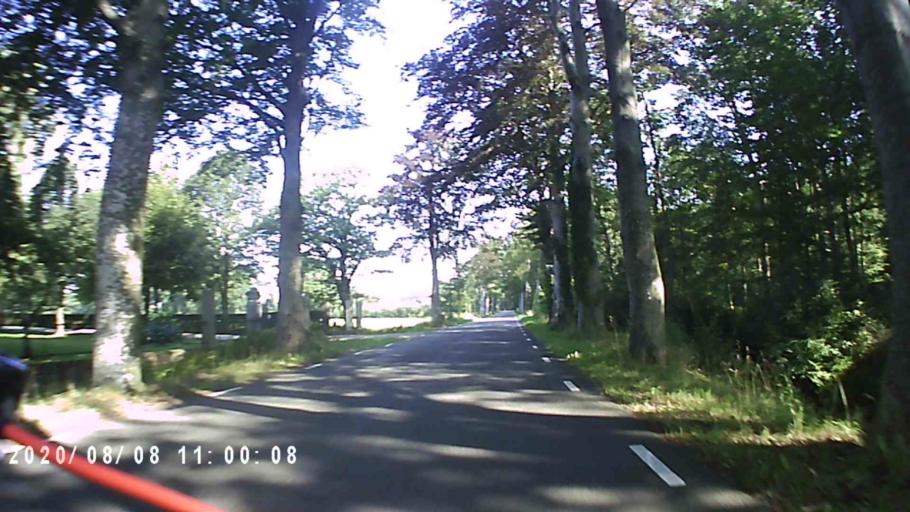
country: NL
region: Groningen
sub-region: Gemeente Leek
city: Leek
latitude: 53.1515
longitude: 6.3950
